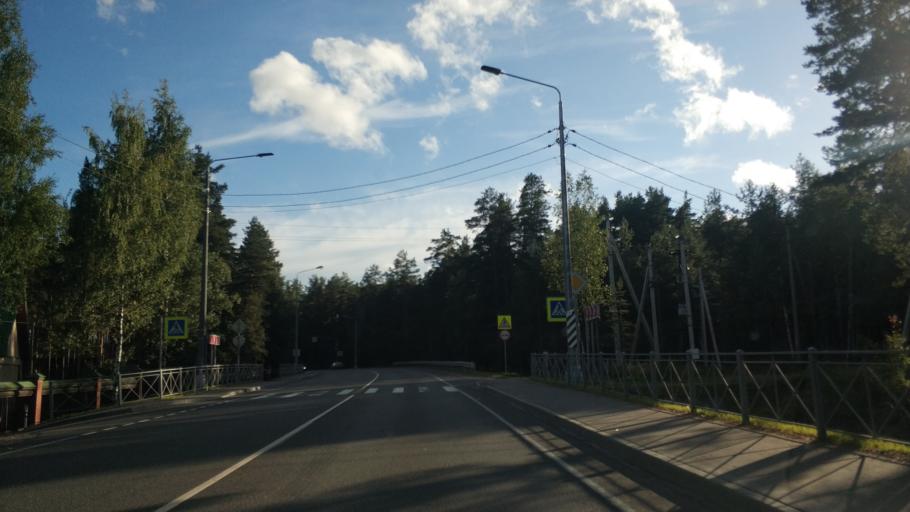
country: RU
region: Leningrad
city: Sapernoye
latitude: 60.7086
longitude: 29.9700
